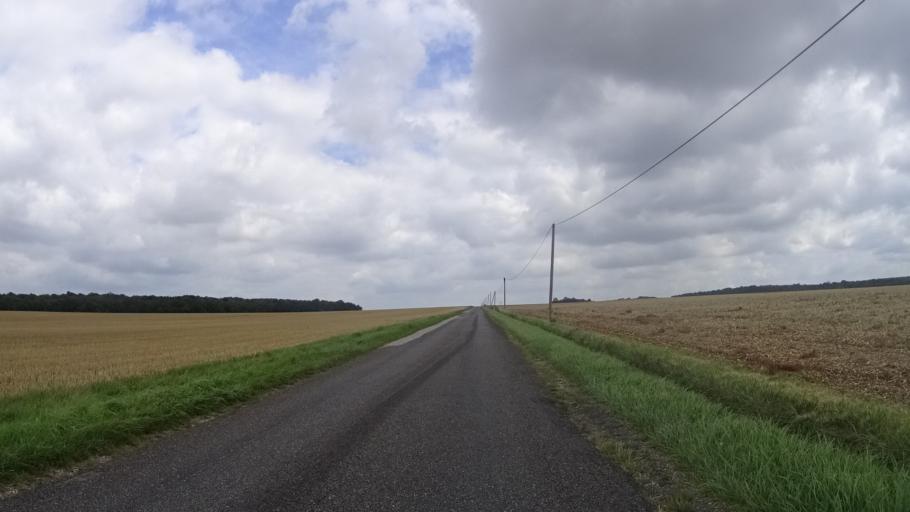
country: FR
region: Lorraine
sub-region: Departement de la Meuse
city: Ligny-en-Barrois
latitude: 48.7555
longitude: 5.4115
